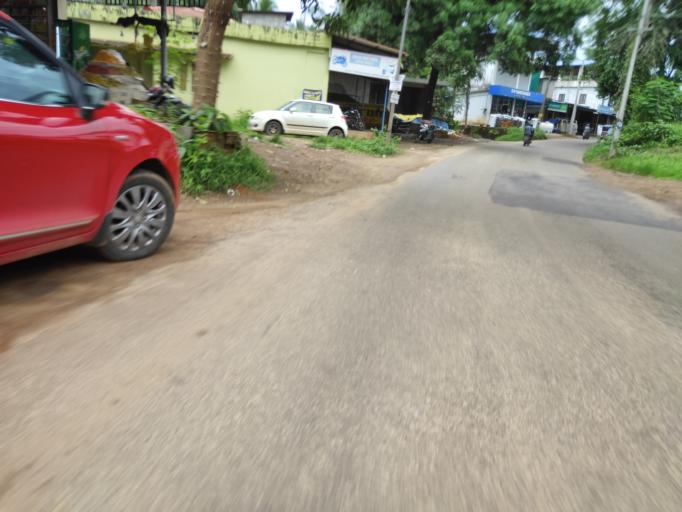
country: IN
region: Kerala
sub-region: Malappuram
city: Manjeri
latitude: 11.1920
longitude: 76.2522
